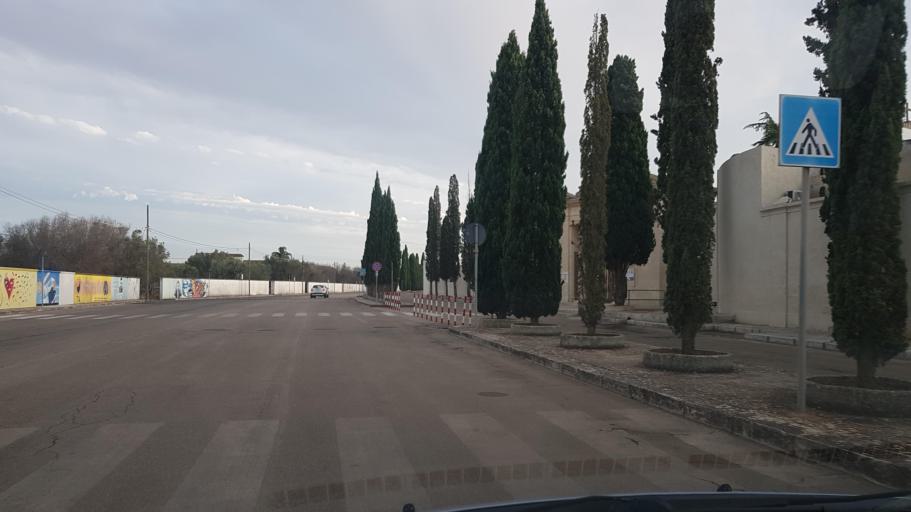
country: IT
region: Apulia
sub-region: Provincia di Lecce
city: Surbo
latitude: 40.4047
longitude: 18.1278
